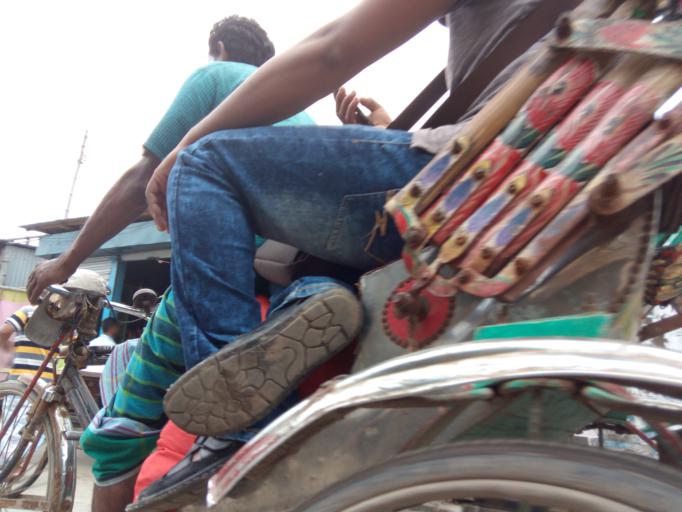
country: BD
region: Dhaka
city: Azimpur
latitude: 23.7185
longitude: 90.3650
